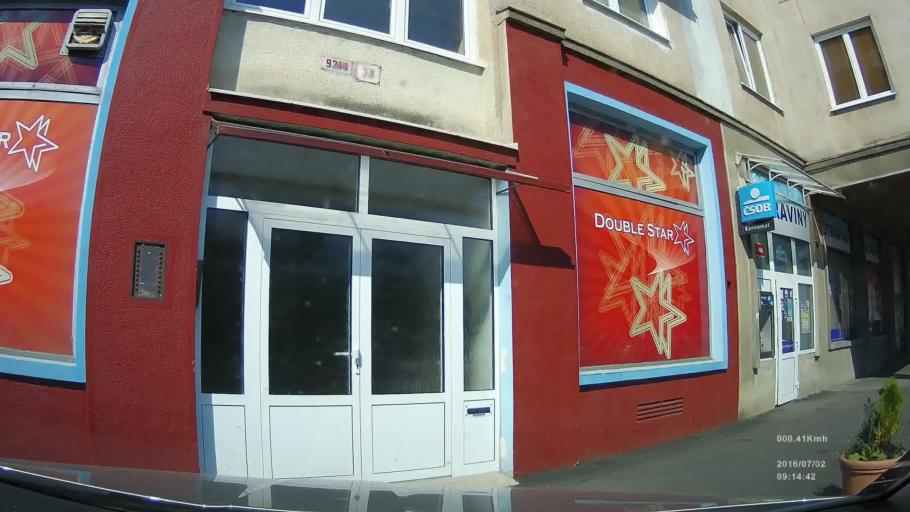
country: SK
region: Kosicky
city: Kosice
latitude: 48.7317
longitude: 21.2448
